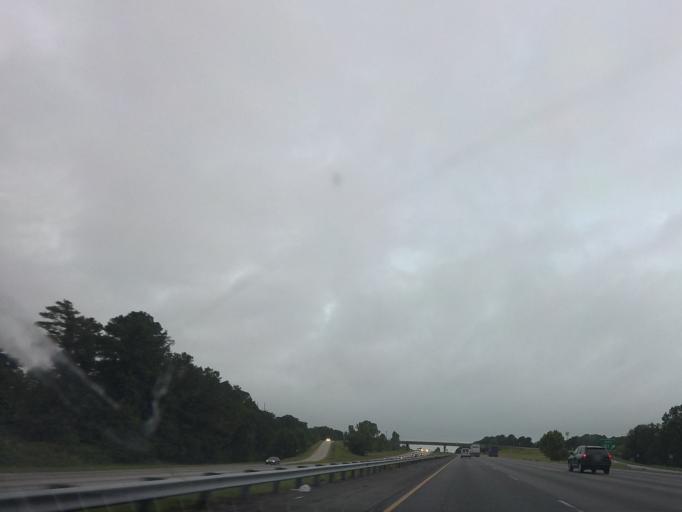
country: US
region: Georgia
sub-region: Monroe County
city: Forsyth
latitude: 32.9892
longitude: -83.8411
